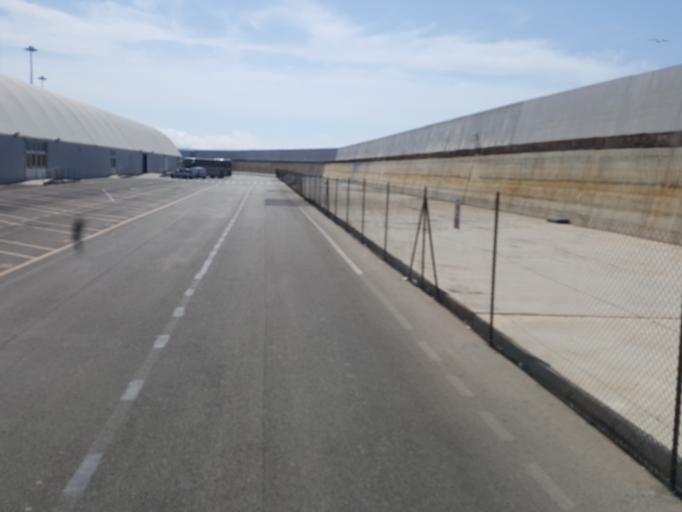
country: IT
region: Latium
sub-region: Citta metropolitana di Roma Capitale
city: Civitavecchia
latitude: 42.0948
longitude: 11.7773
